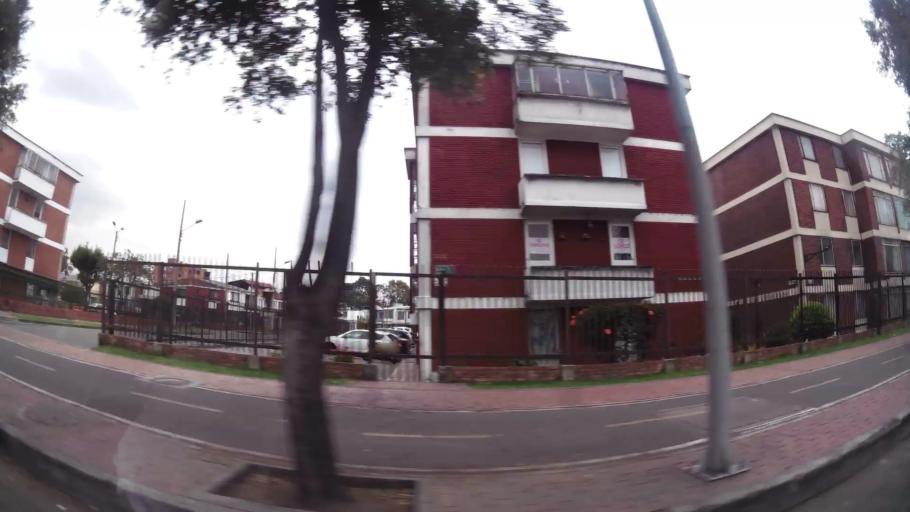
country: CO
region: Bogota D.C.
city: Barrio San Luis
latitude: 4.6727
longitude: -74.0662
